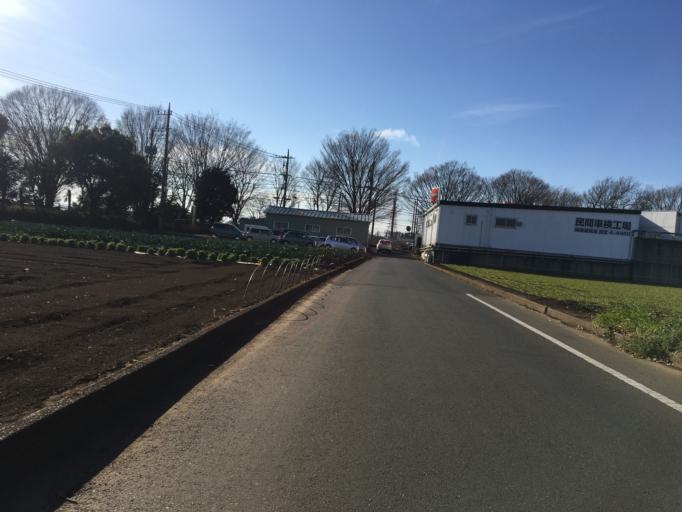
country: JP
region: Saitama
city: Oi
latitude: 35.8242
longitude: 139.5385
